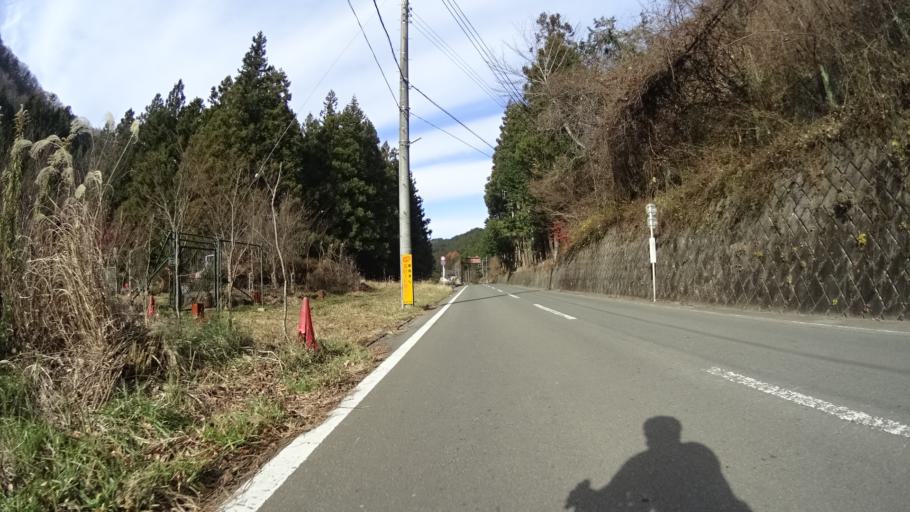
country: JP
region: Yamanashi
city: Otsuki
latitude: 35.5248
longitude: 138.9245
